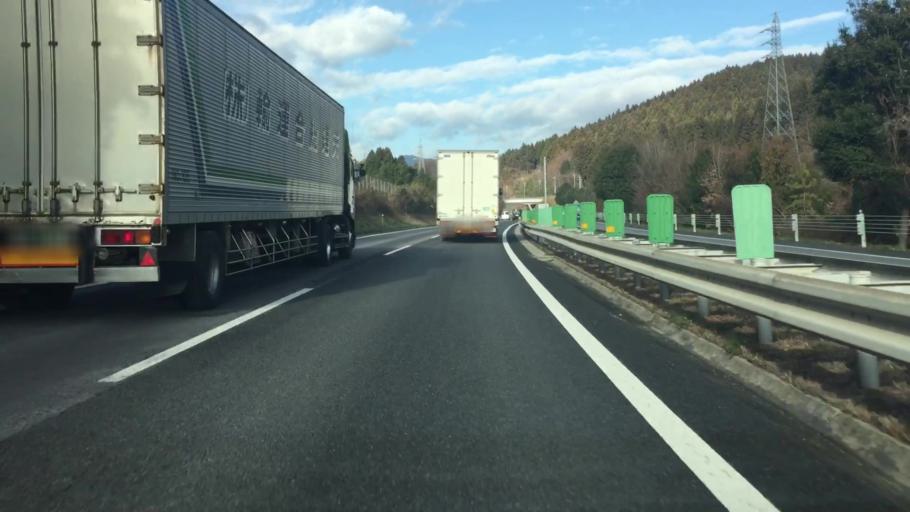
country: JP
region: Gunma
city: Annaka
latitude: 36.3348
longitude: 138.7496
